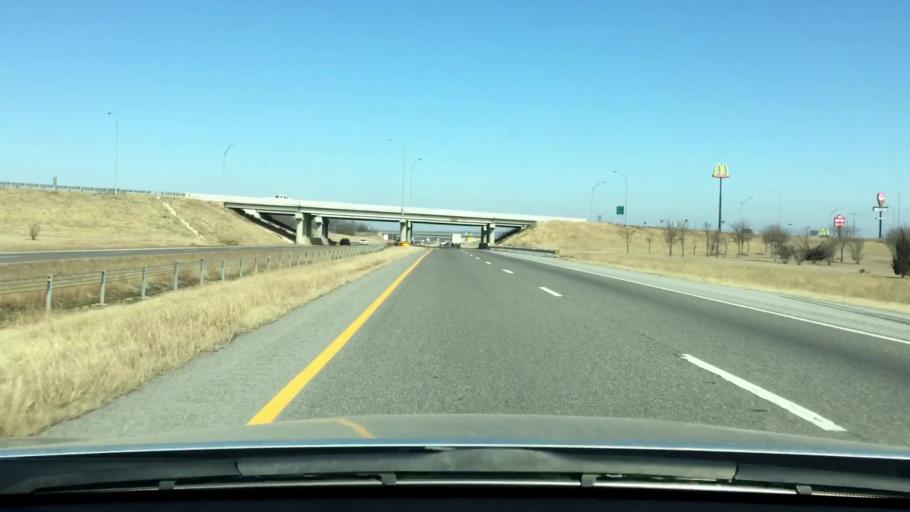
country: US
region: Oklahoma
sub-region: McClain County
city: Purcell
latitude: 34.9810
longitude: -97.3723
